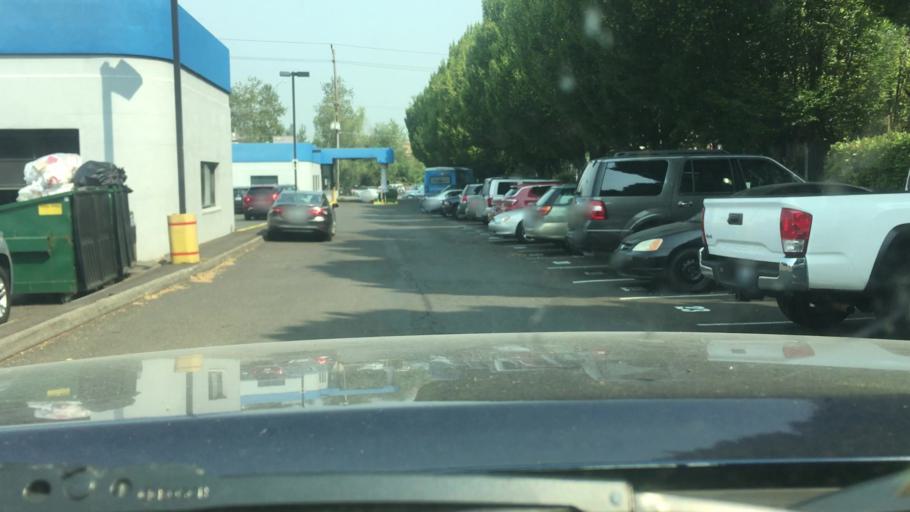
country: US
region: Oregon
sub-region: Multnomah County
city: Lents
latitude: 45.5671
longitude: -122.5512
